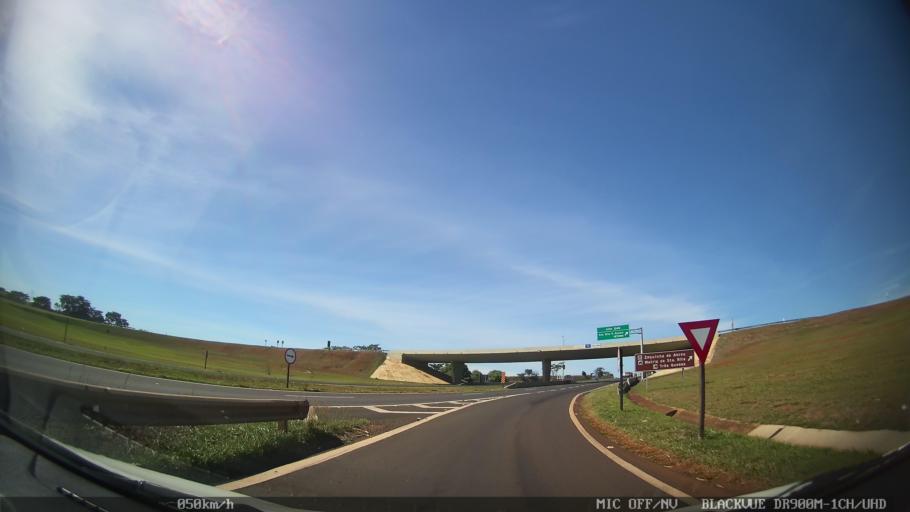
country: BR
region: Sao Paulo
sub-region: Santa Rita Do Passa Quatro
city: Santa Rita do Passa Quatro
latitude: -21.7557
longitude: -47.5650
